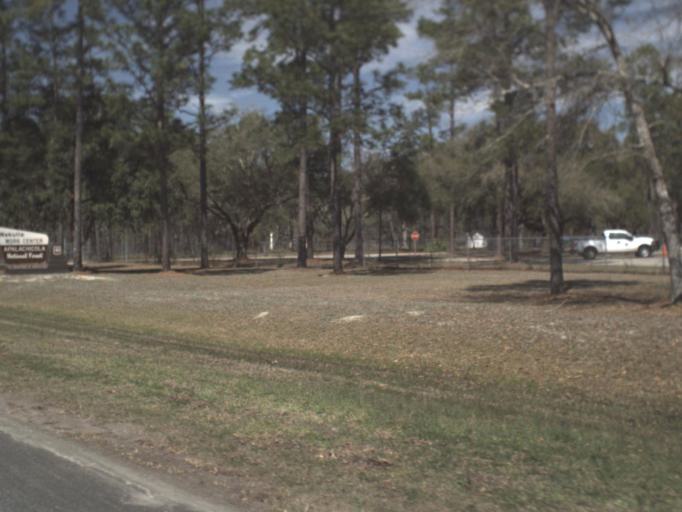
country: US
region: Florida
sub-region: Wakulla County
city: Crawfordville
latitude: 30.3043
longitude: -84.4241
